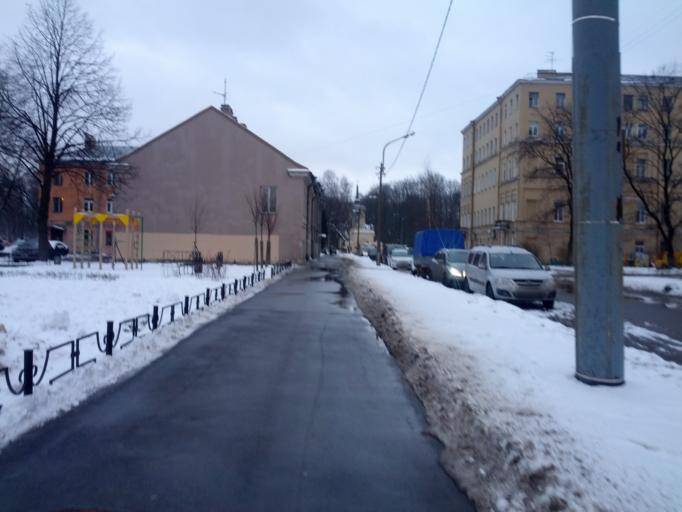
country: RU
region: St.-Petersburg
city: Centralniy
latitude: 59.9054
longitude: 30.3551
